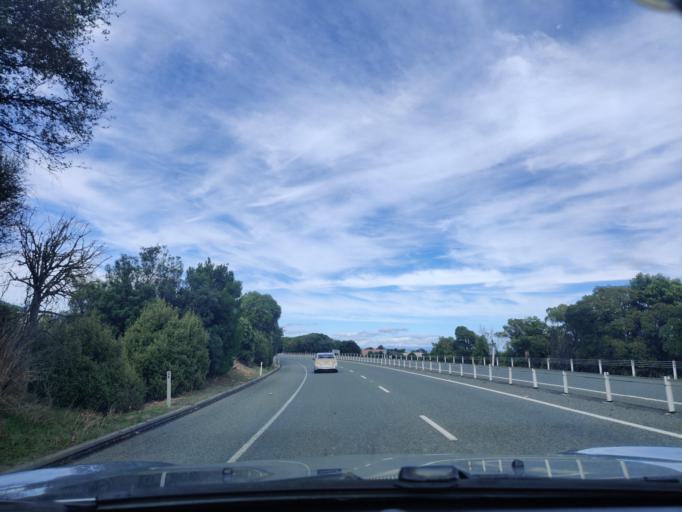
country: NZ
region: Tasman
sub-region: Tasman District
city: Richmond
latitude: -41.3025
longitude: 173.2256
